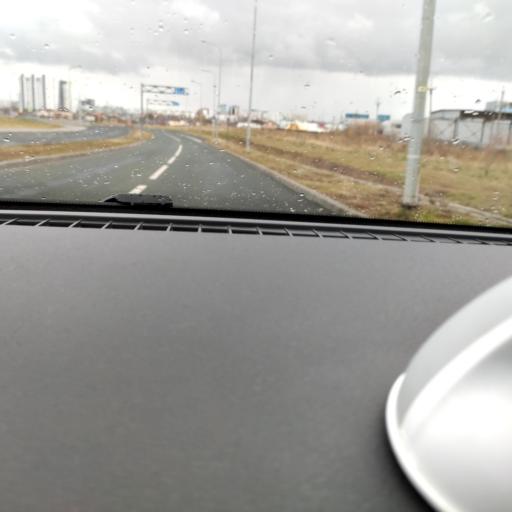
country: RU
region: Samara
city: Samara
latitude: 53.2773
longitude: 50.2320
